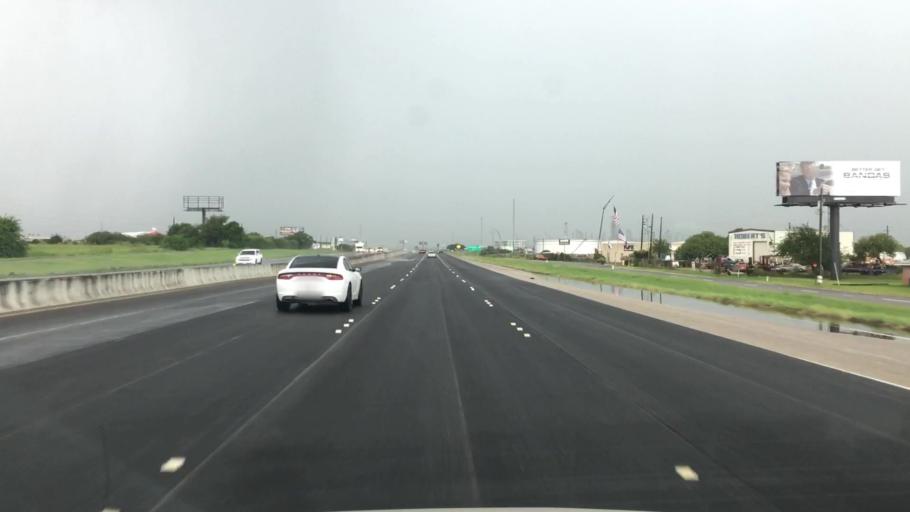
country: US
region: Texas
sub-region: Nueces County
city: Corpus Christi
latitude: 27.8142
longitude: -97.5085
